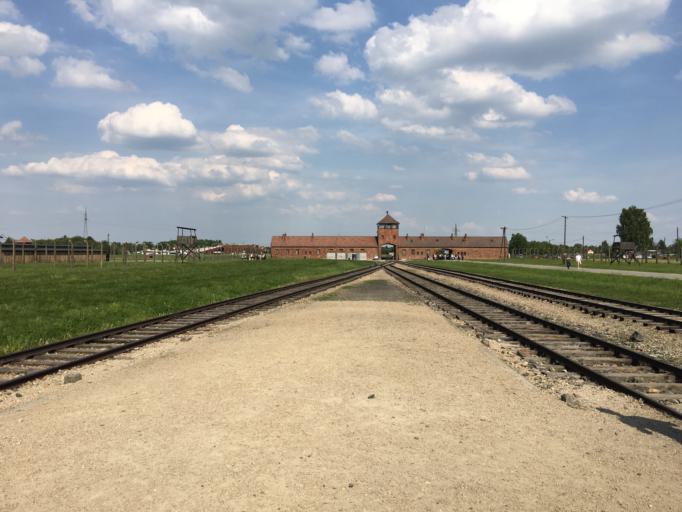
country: PL
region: Lesser Poland Voivodeship
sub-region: Powiat oswiecimski
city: Brzezinka
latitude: 50.0347
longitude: 19.1784
